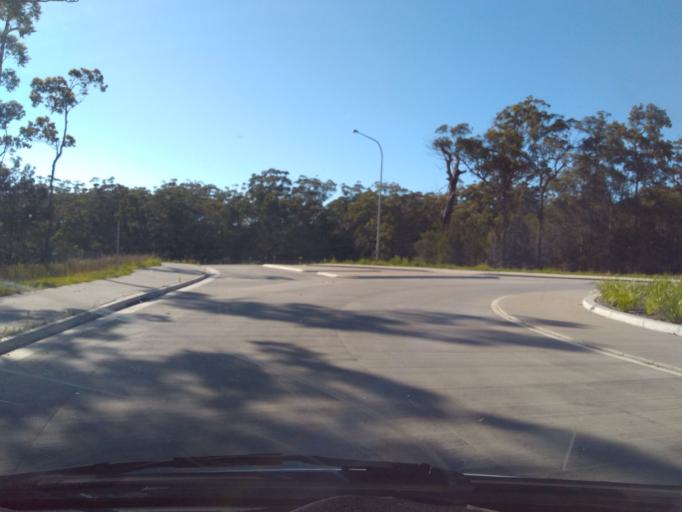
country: AU
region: New South Wales
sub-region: Port Macquarie-Hastings
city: Port Macquarie
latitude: -31.4464
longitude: 152.8250
